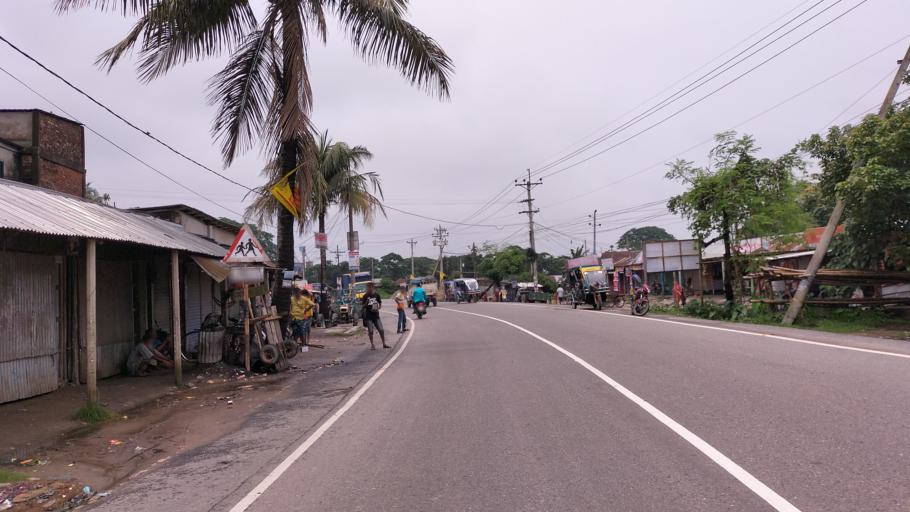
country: BD
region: Dhaka
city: Netrakona
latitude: 24.8492
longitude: 90.6439
